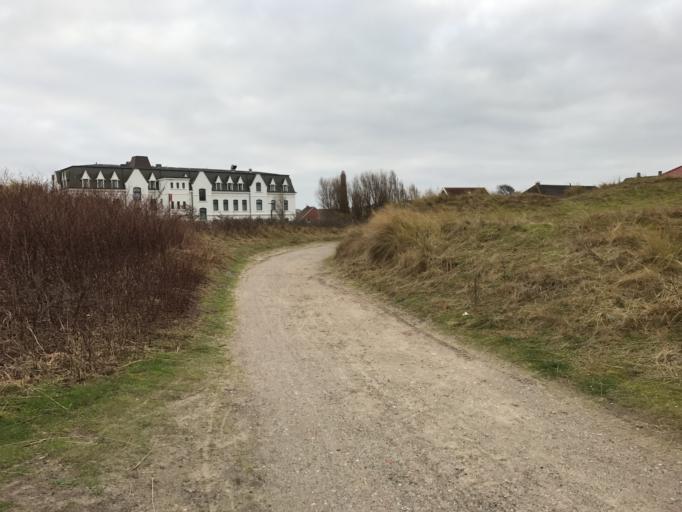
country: DE
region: Lower Saxony
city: Borkum
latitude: 53.5942
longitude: 6.6666
